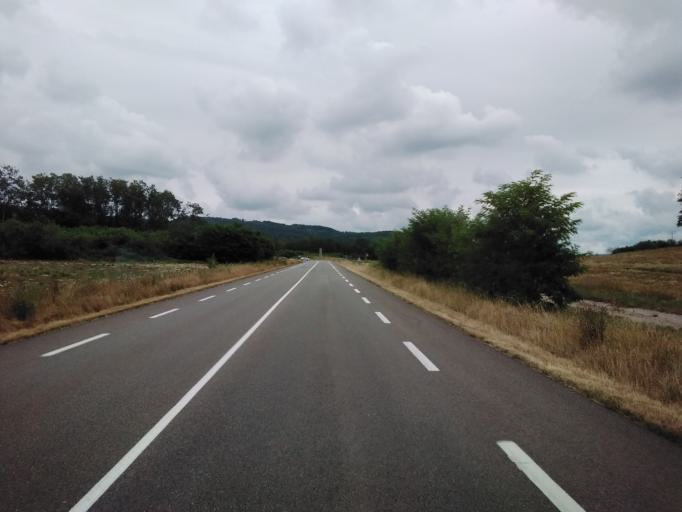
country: FR
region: Franche-Comte
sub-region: Departement du Jura
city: Montmorot
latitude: 46.6547
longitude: 5.5079
